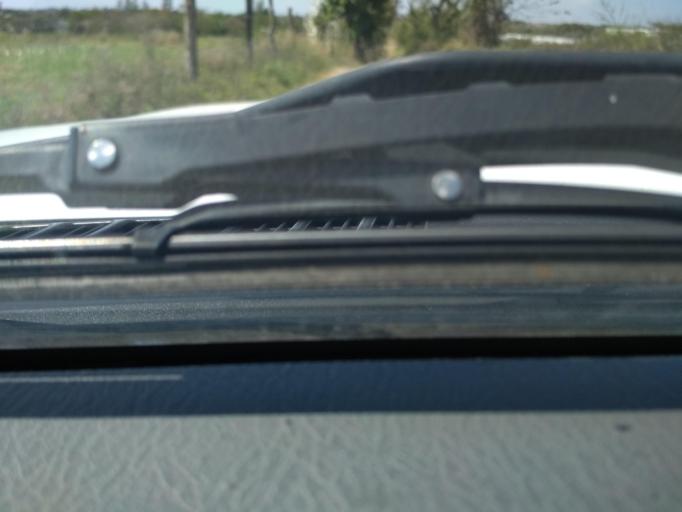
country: MX
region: Veracruz
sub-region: Veracruz
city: Las Amapolas
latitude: 19.1377
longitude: -96.2244
